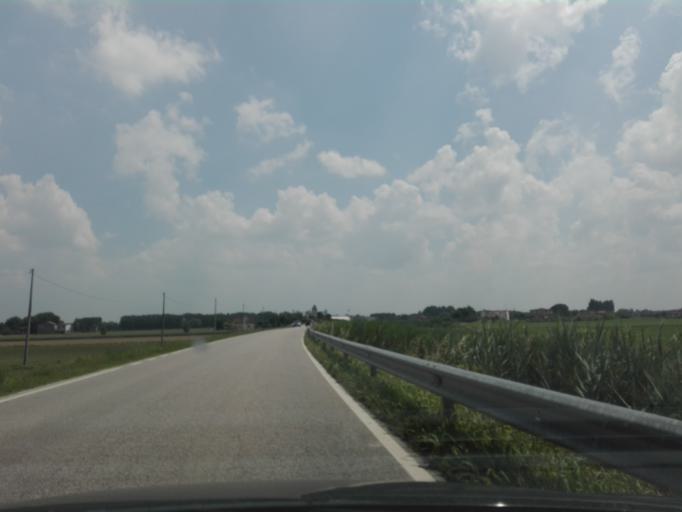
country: IT
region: Veneto
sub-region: Provincia di Rovigo
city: Adria
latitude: 45.0583
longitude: 12.0180
